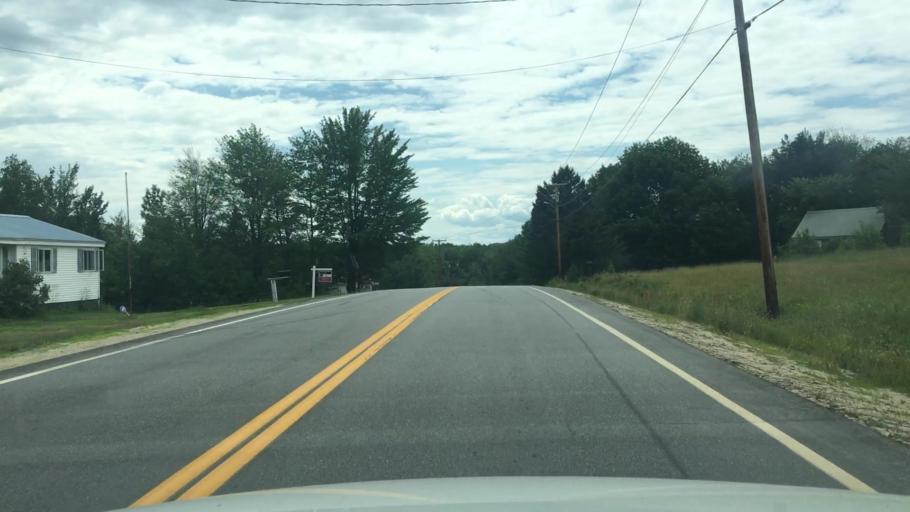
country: US
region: Maine
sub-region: Oxford County
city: West Paris
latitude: 44.3664
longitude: -70.4813
